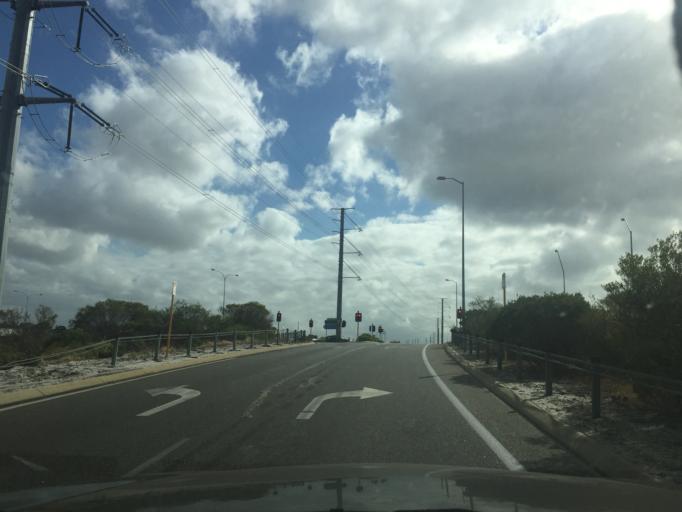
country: AU
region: Western Australia
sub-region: Canning
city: Canning Vale
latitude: -32.0572
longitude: 115.9057
